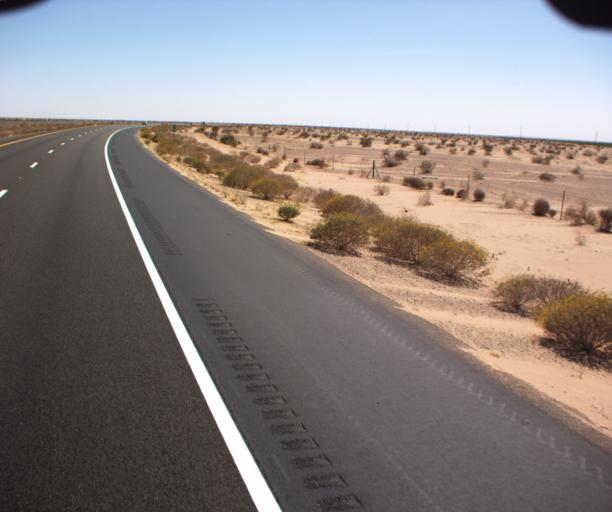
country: US
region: Arizona
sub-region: Yuma County
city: Somerton
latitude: 32.5078
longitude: -114.5586
